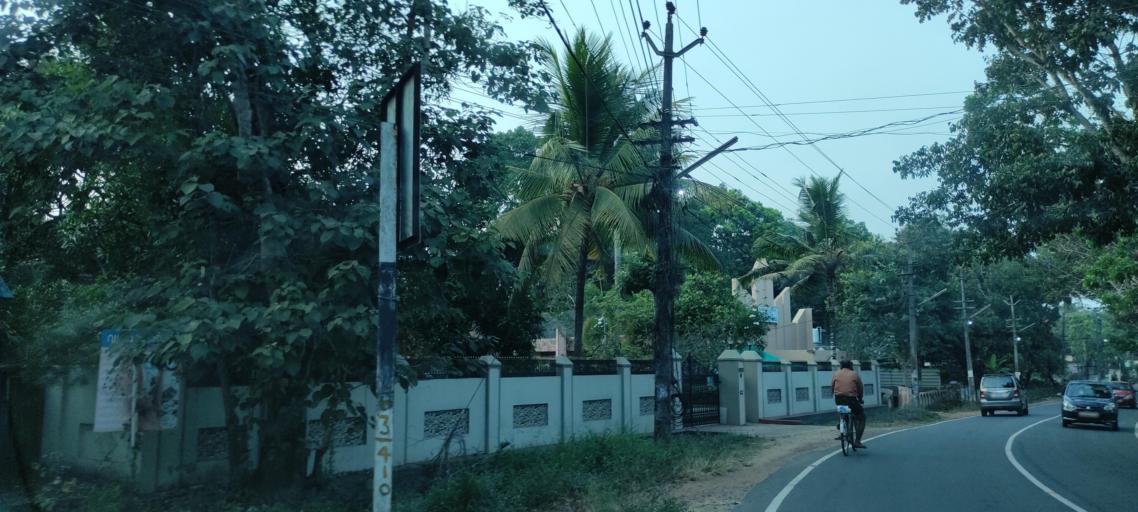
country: IN
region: Kerala
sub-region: Alappuzha
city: Mavelikara
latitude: 9.2722
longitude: 76.5360
